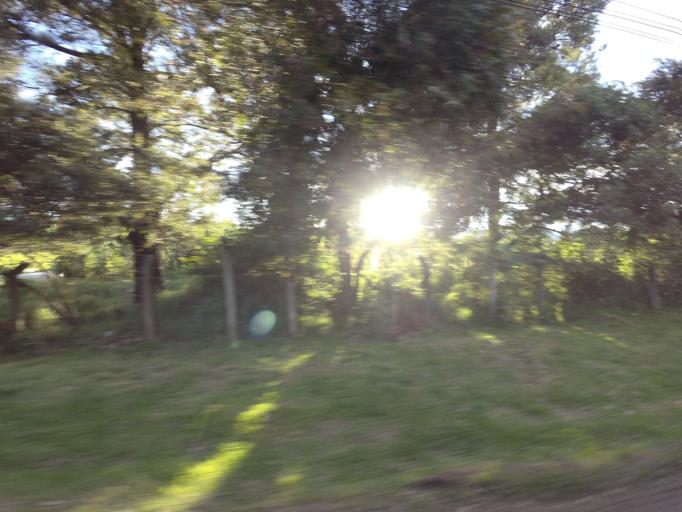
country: CO
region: Cundinamarca
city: Chia
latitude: 4.8014
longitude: -74.0304
